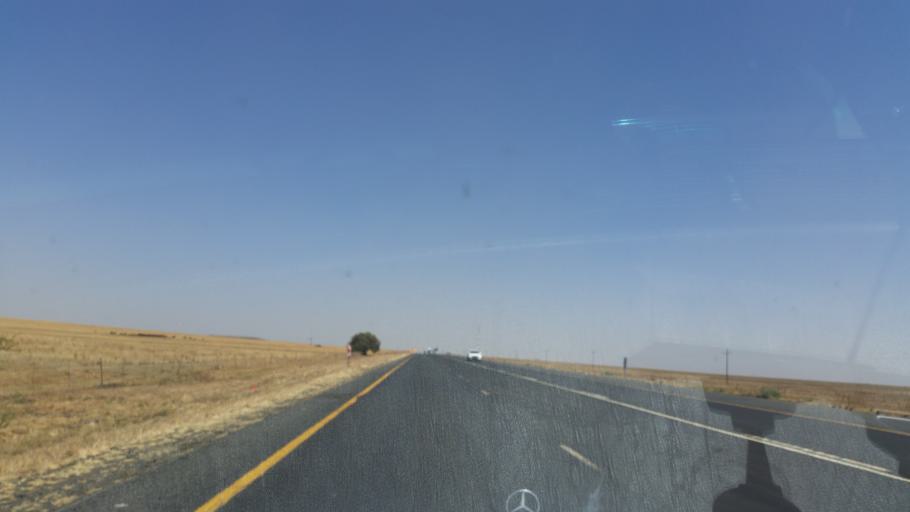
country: ZA
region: Orange Free State
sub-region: Lejweleputswa District Municipality
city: Brandfort
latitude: -28.8053
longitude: 26.6820
